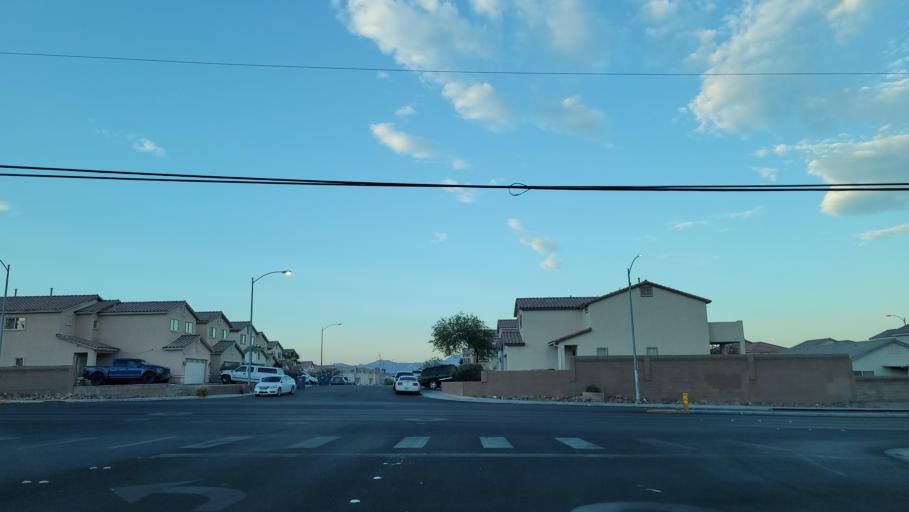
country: US
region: Nevada
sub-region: Clark County
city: Sunrise Manor
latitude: 36.1598
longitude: -115.0355
